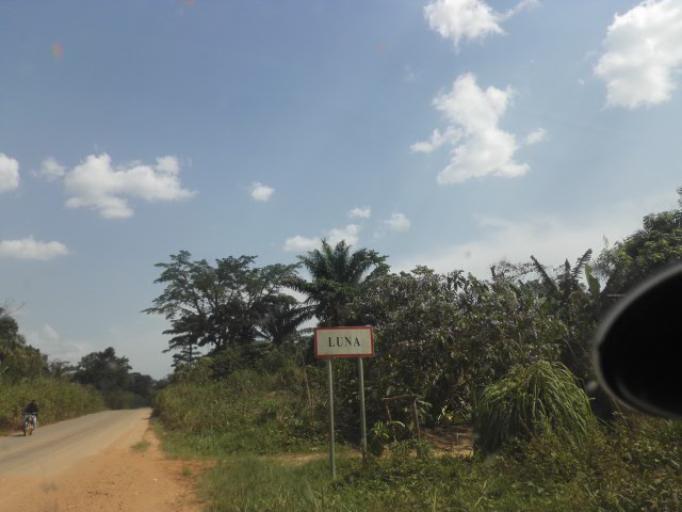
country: CD
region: Nord Kivu
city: Beni
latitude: 0.9086
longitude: 29.6142
